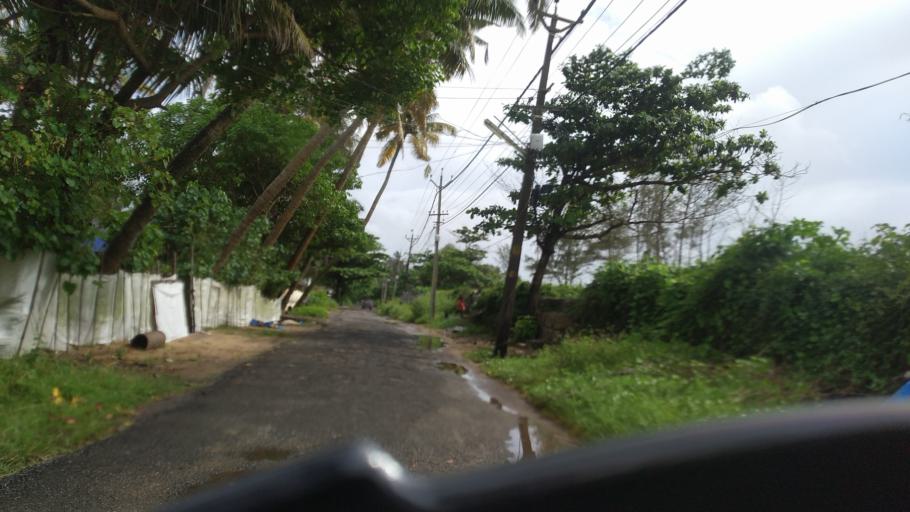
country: IN
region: Kerala
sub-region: Thrissur District
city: Kodungallur
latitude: 10.1305
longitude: 76.1821
